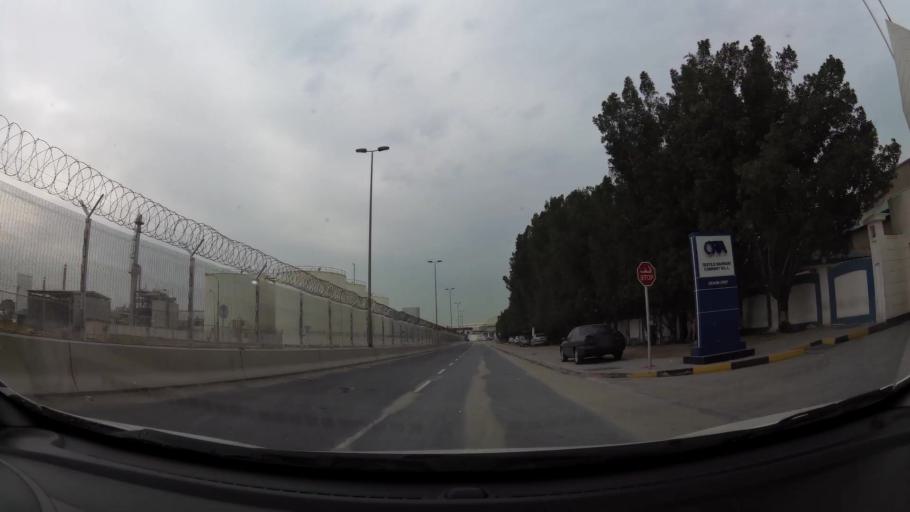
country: BH
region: Northern
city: Sitrah
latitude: 26.1850
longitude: 50.6133
